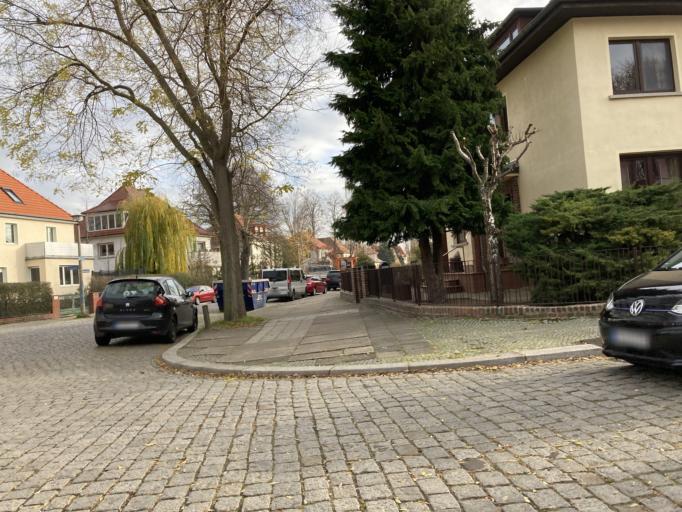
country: DE
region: Saxony-Anhalt
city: Magdeburg
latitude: 52.1366
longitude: 11.6220
